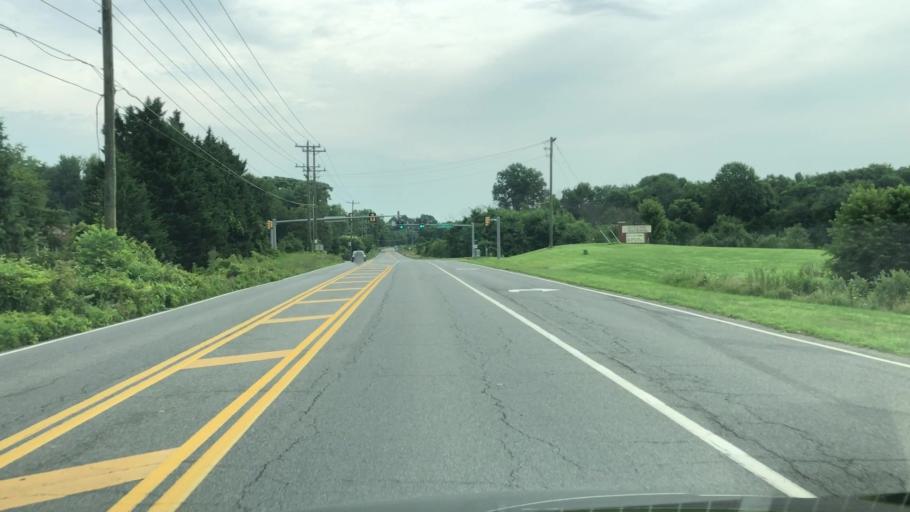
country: US
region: Virginia
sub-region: Fauquier County
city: New Baltimore
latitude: 38.7346
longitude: -77.6850
